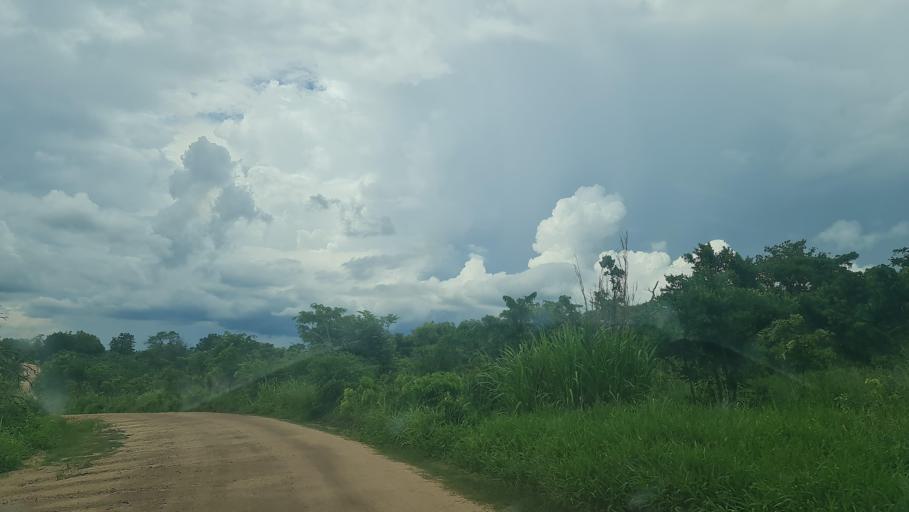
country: MW
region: Southern Region
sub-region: Nsanje District
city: Nsanje
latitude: -17.5898
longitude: 35.6732
